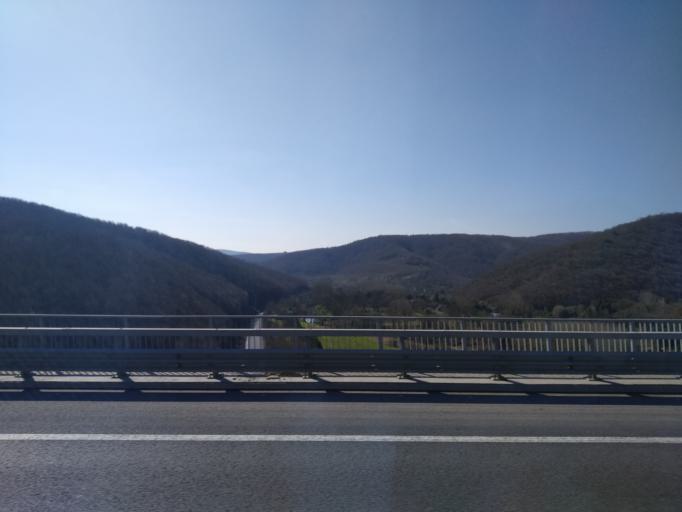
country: TR
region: Istanbul
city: Mahmut Sevket Pasa
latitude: 41.1527
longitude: 29.2685
